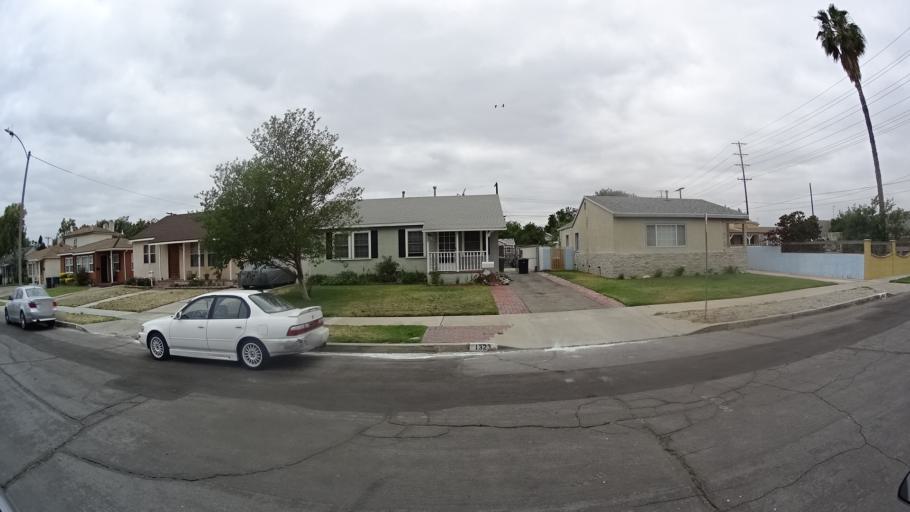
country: US
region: California
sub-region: Los Angeles County
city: Burbank
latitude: 34.1872
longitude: -118.3271
